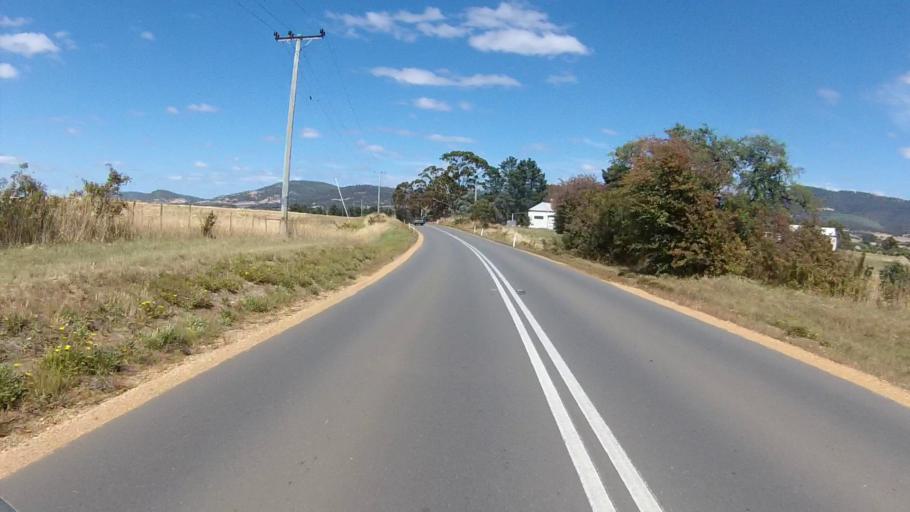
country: AU
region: Tasmania
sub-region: Clarence
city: Cambridge
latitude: -42.7486
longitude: 147.4172
